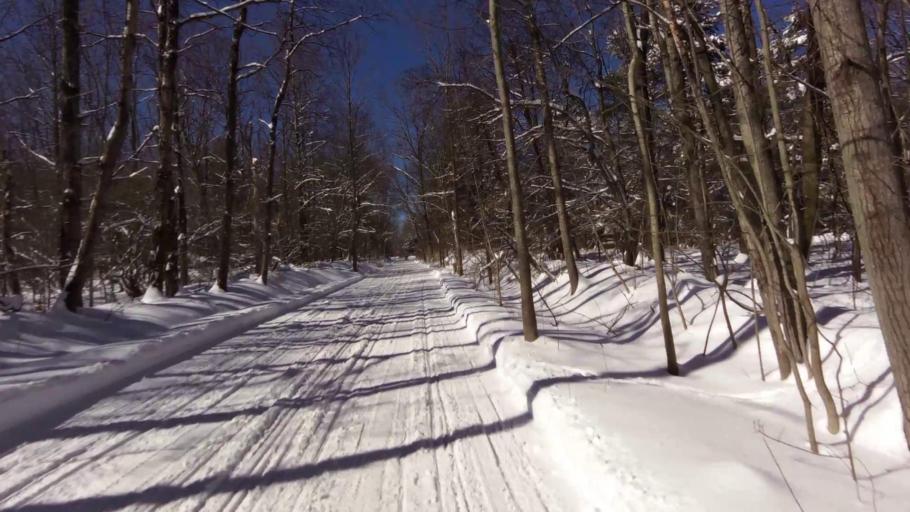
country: US
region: New York
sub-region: Chautauqua County
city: Mayville
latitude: 42.2357
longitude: -79.5091
